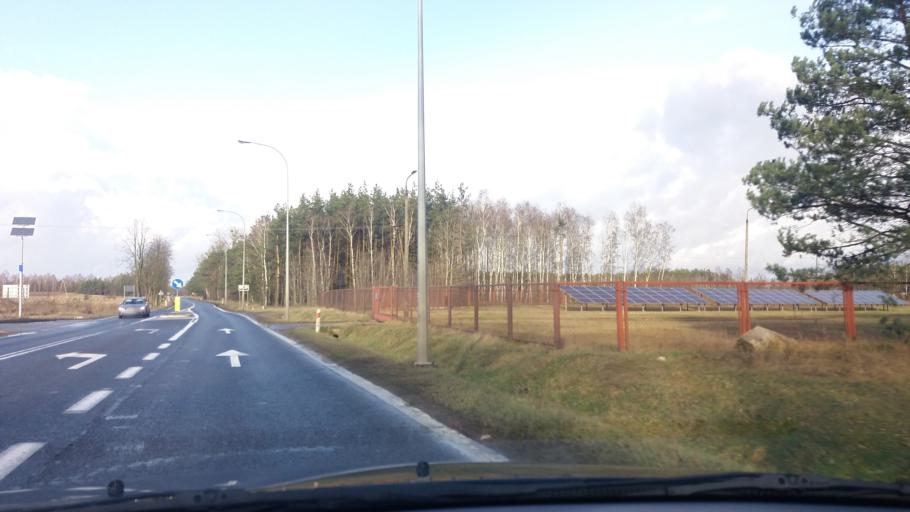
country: PL
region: Masovian Voivodeship
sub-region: Powiat przasnyski
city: Chorzele
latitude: 53.2678
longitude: 20.8979
